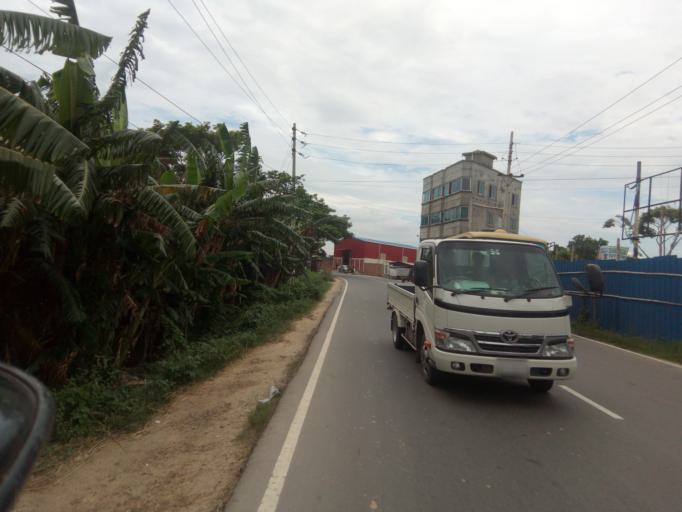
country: BD
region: Dhaka
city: Paltan
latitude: 23.7364
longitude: 90.4835
